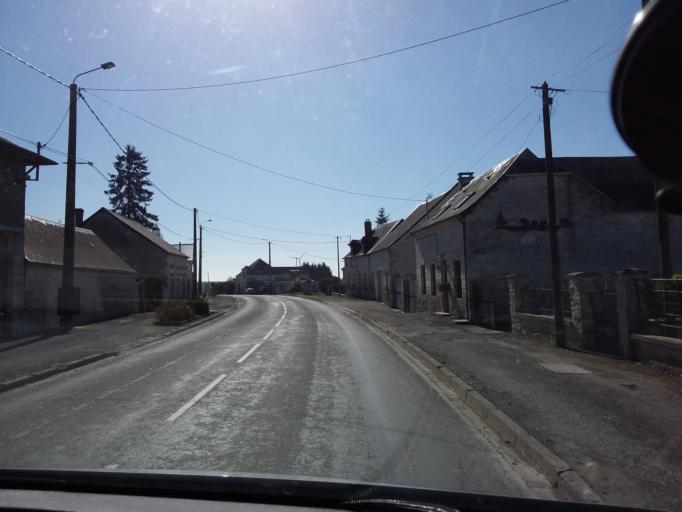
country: FR
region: Picardie
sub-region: Departement de l'Aisne
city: Montcornet
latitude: 49.6254
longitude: 4.0229
